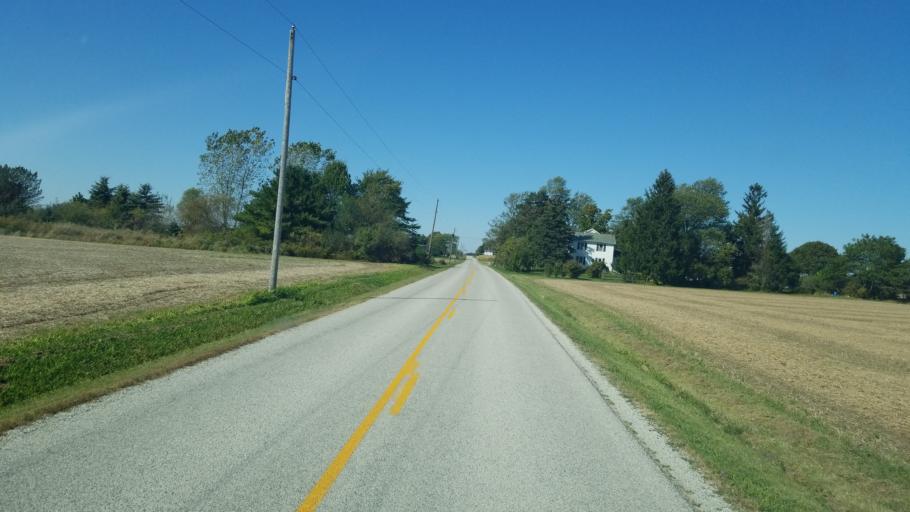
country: US
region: Ohio
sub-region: Richland County
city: Shelby
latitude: 40.8900
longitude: -82.6965
